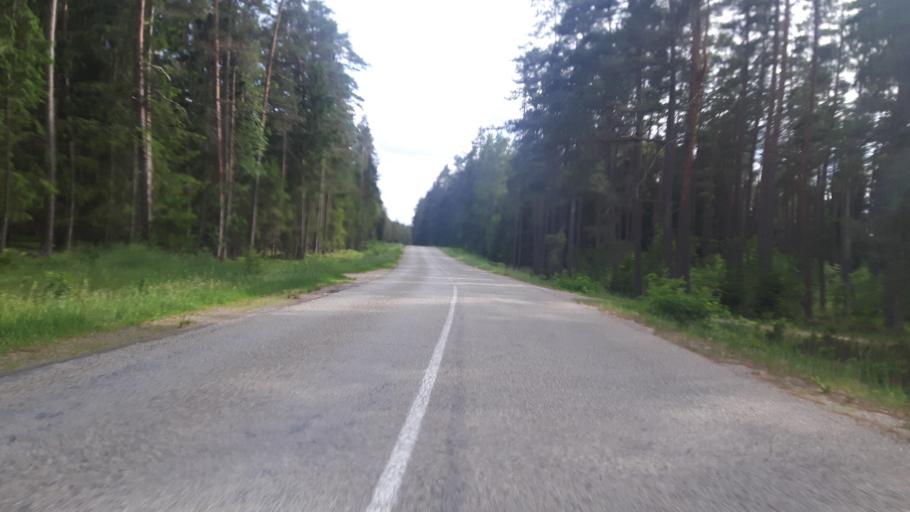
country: LV
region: Engure
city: Smarde
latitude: 57.0073
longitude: 23.3356
